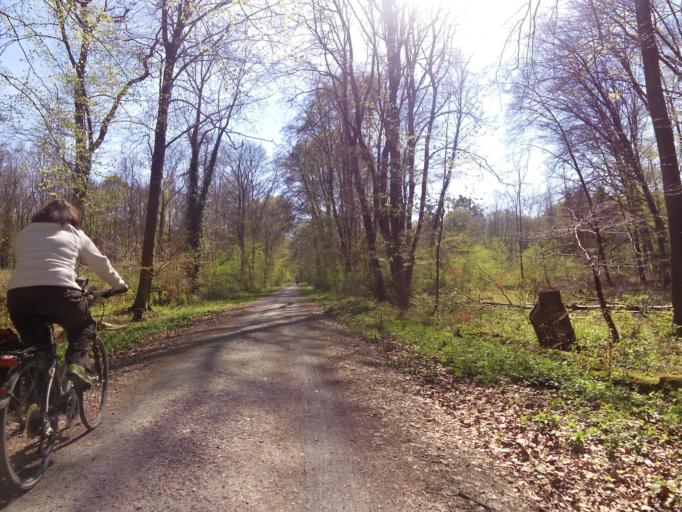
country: DE
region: Hesse
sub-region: Regierungsbezirk Darmstadt
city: Nauheim
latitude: 49.9758
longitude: 8.5072
